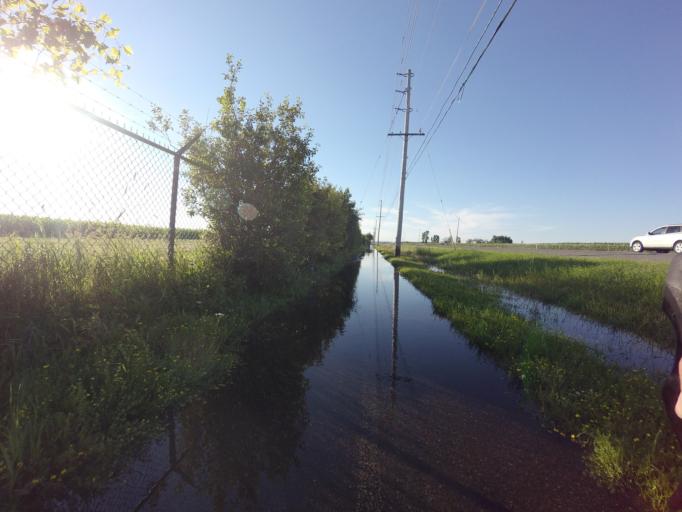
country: CA
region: Ontario
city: Bells Corners
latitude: 45.2978
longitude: -75.7630
